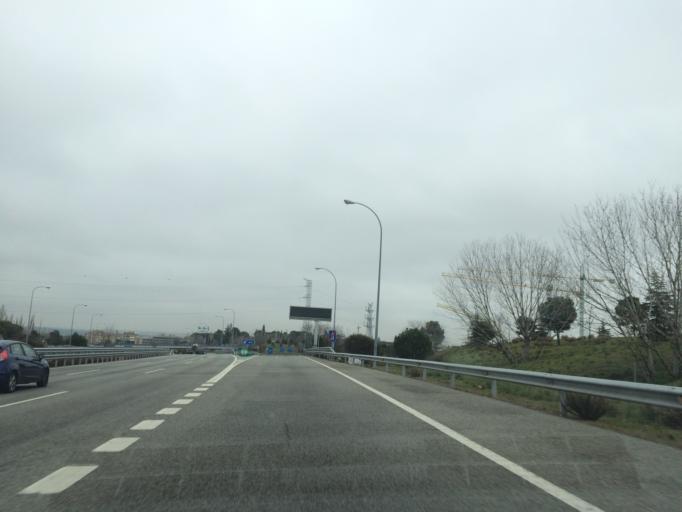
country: ES
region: Madrid
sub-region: Provincia de Madrid
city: Pozuelo de Alarcon
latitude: 40.4618
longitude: -3.8015
